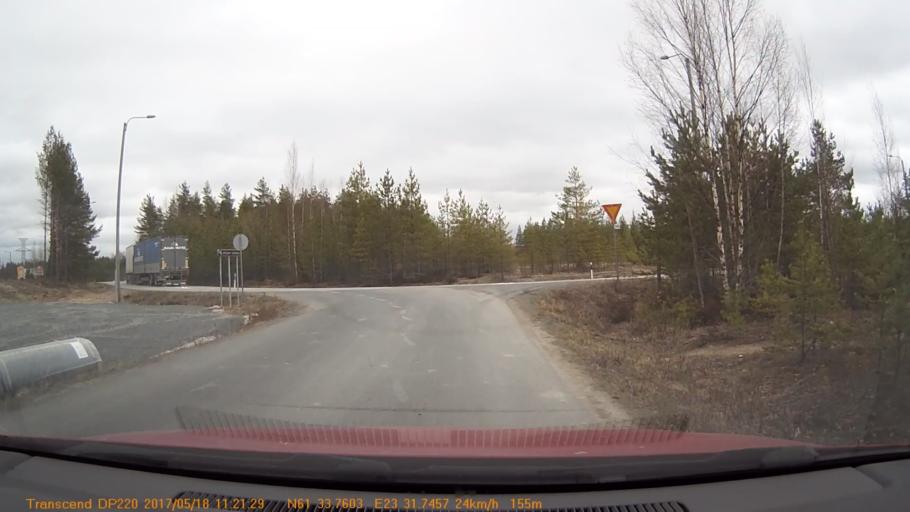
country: FI
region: Pirkanmaa
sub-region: Tampere
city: Yloejaervi
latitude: 61.5628
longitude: 23.5289
